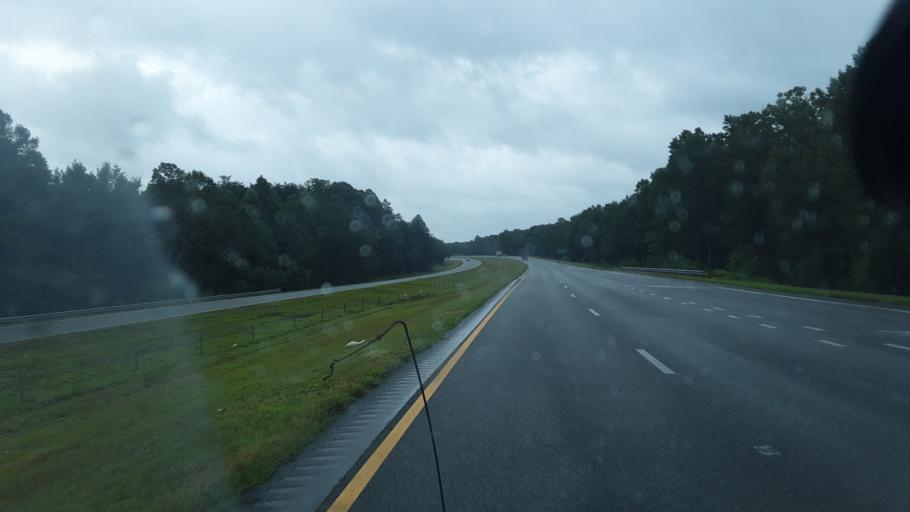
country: US
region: North Carolina
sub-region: Guilford County
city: High Point
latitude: 36.0232
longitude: -80.0526
